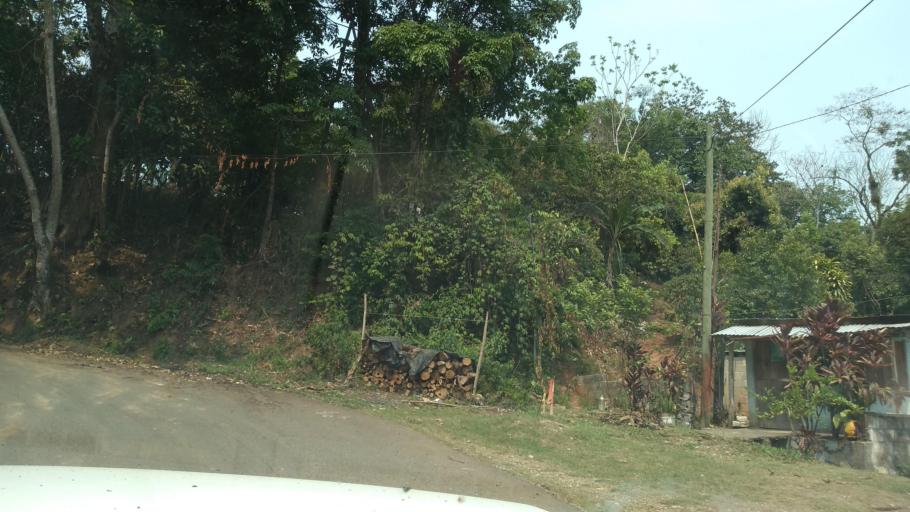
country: MX
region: Veracruz
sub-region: Tezonapa
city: Laguna Chica (Pueblo Nuevo)
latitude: 18.5310
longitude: -96.7885
